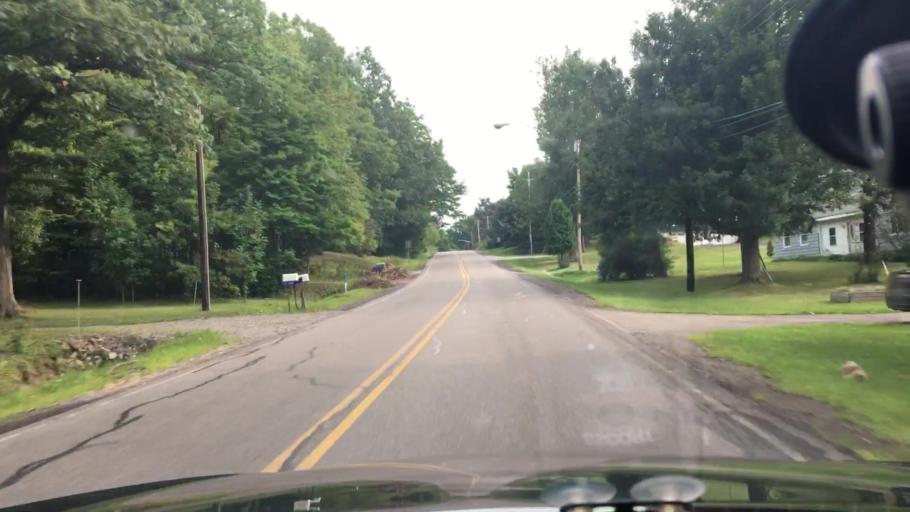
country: US
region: New York
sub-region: Erie County
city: Orchard Park
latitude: 42.7320
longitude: -78.7322
